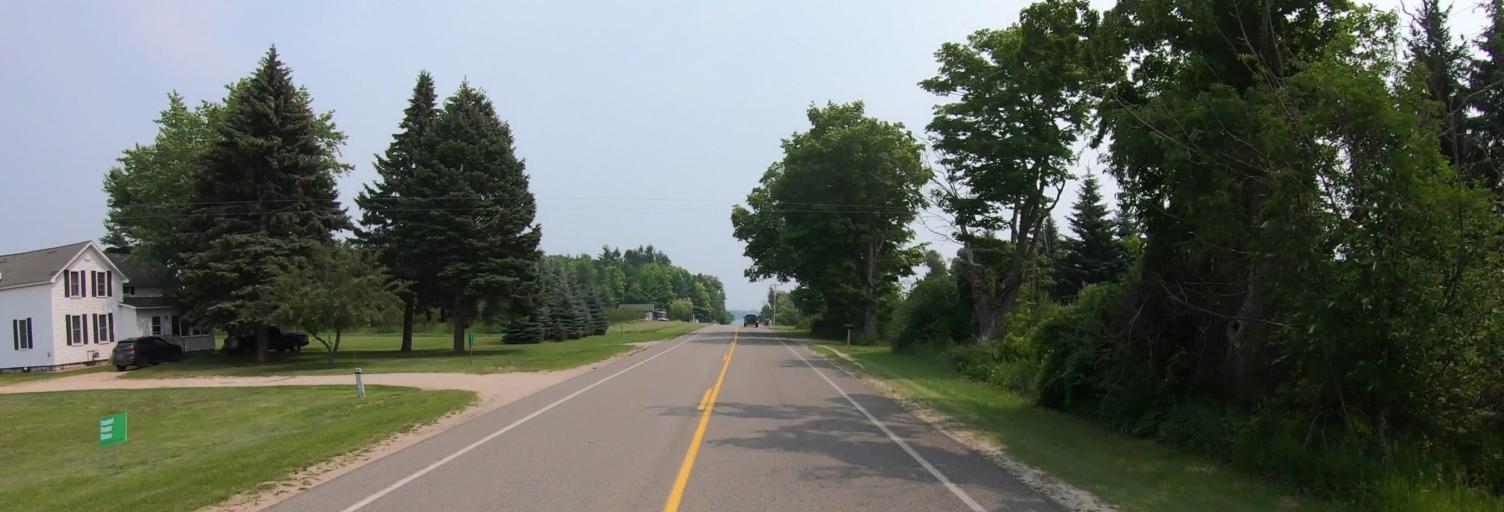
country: US
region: Michigan
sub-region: Leelanau County
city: Leland
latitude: 45.1510
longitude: -85.6061
